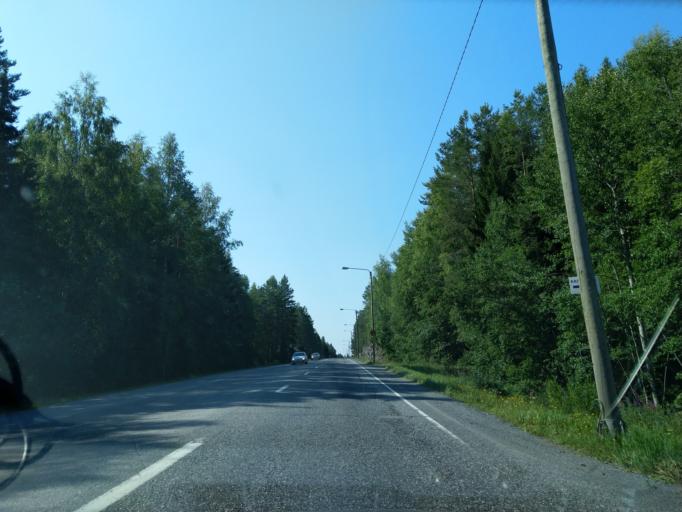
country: FI
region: Satakunta
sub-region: Pori
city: Noormarkku
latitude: 61.5904
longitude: 21.8563
